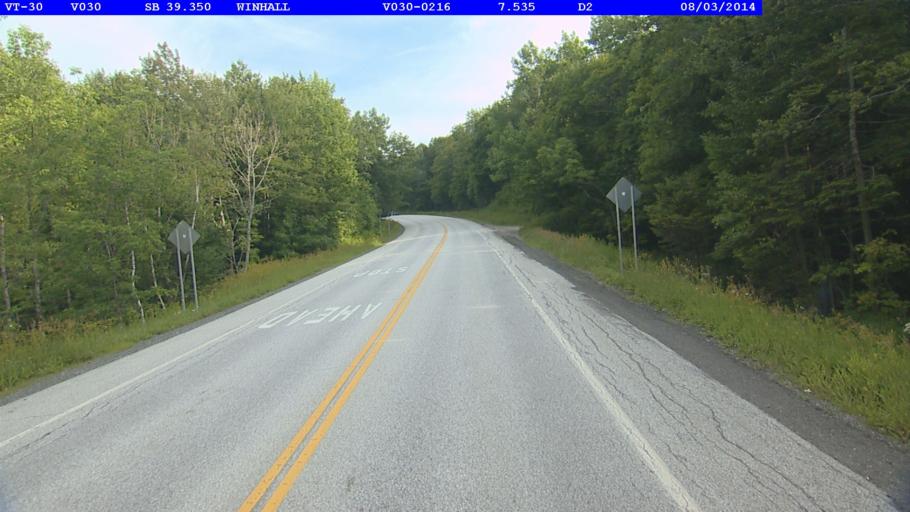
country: US
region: Vermont
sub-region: Bennington County
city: Manchester Center
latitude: 43.2040
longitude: -72.9604
